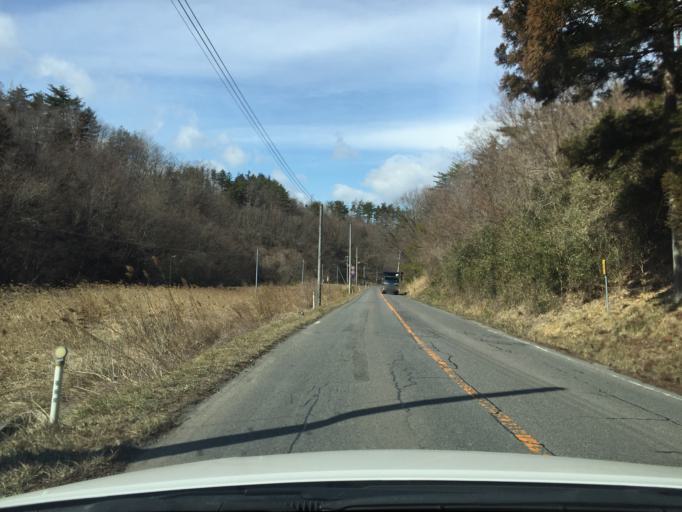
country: JP
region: Fukushima
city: Funehikimachi-funehiki
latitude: 37.4031
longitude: 140.5492
